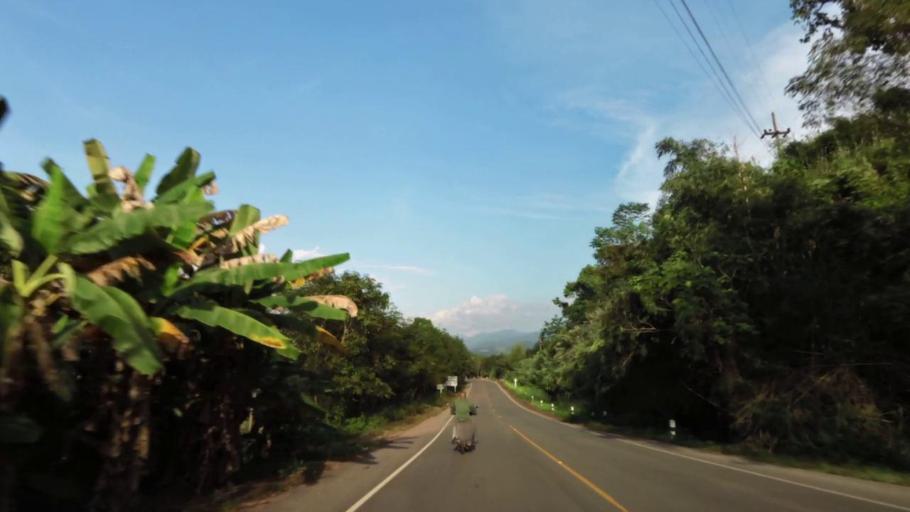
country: TH
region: Chiang Rai
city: Khun Tan
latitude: 19.8539
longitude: 100.3849
